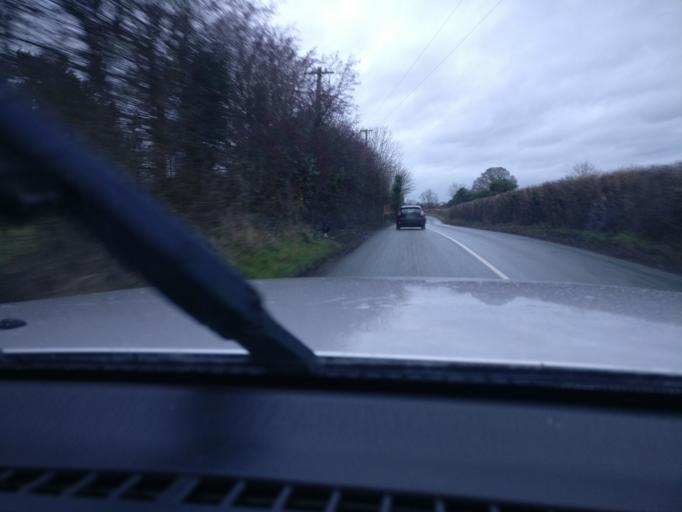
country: IE
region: Leinster
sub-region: An Mhi
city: Longwood
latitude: 53.4509
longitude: -6.9609
